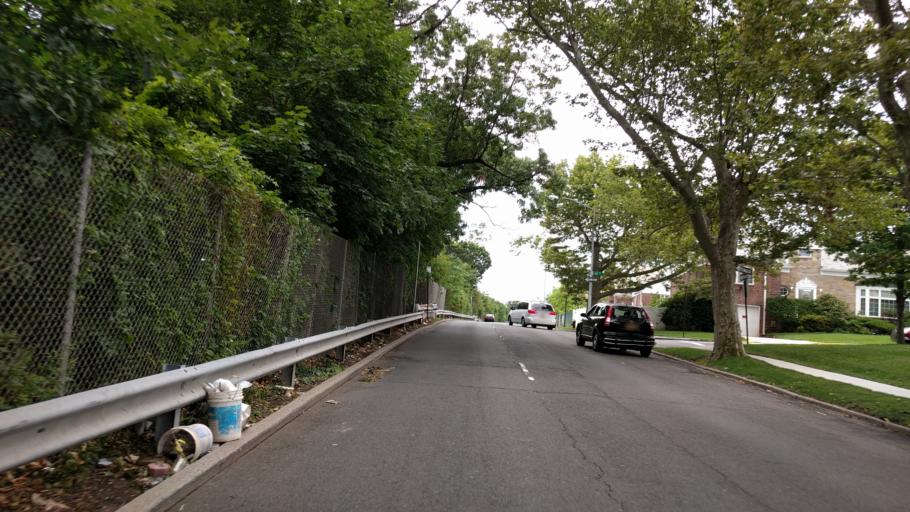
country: US
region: New York
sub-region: Queens County
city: Borough of Queens
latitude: 40.7285
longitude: -73.8401
